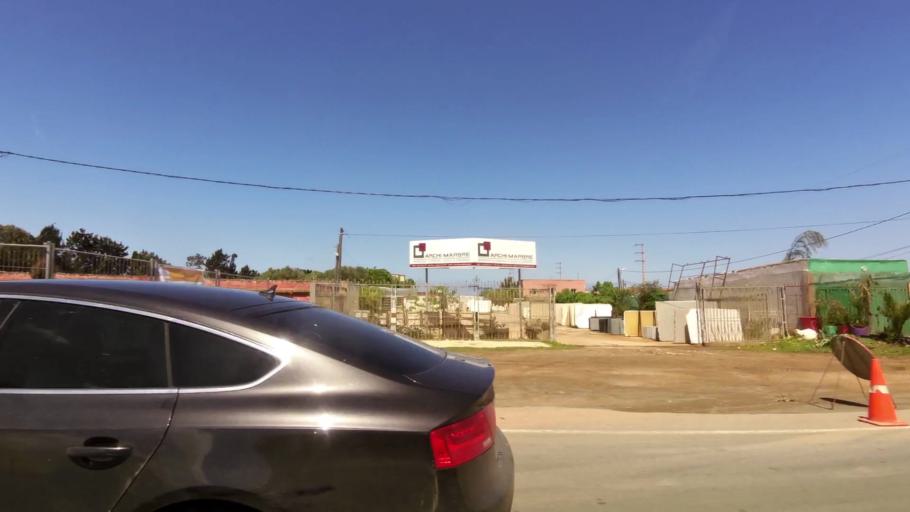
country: MA
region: Grand Casablanca
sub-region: Nouaceur
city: Dar Bouazza
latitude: 33.5178
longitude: -7.8002
